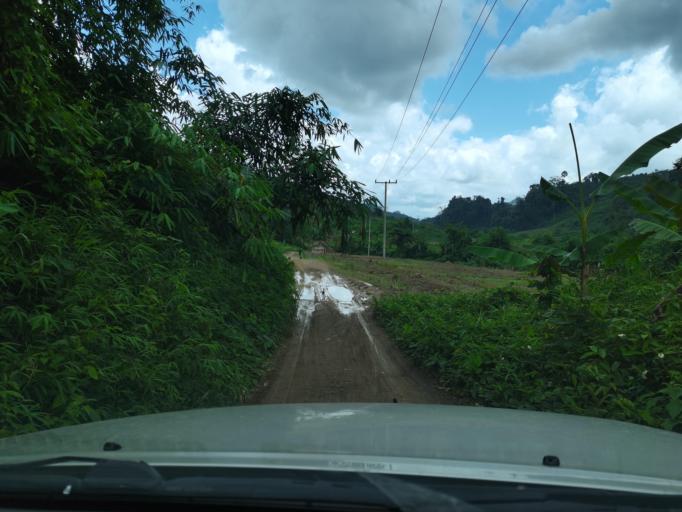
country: LA
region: Loungnamtha
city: Muang Long
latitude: 20.7659
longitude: 101.0176
